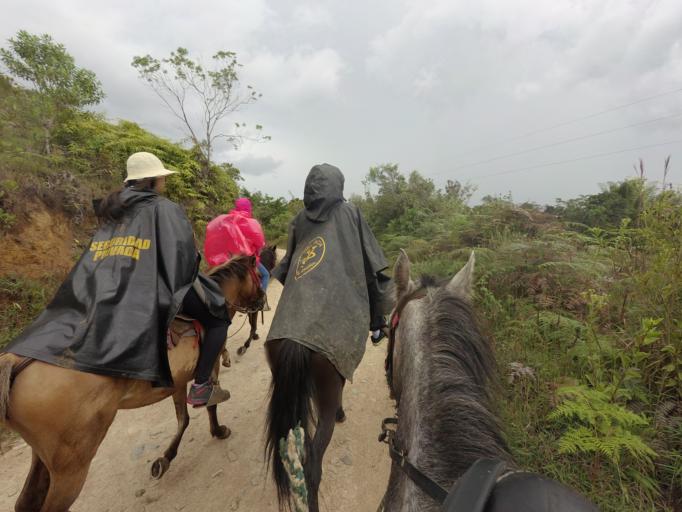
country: CO
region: Huila
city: San Agustin
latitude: 1.9006
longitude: -76.2945
